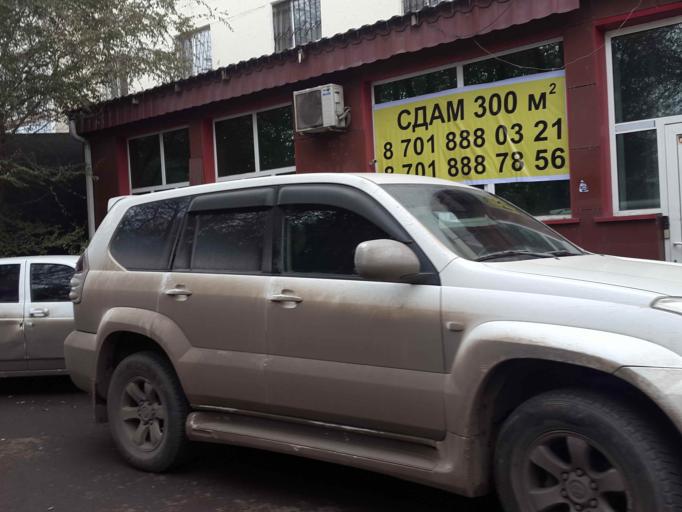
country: KZ
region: Astana Qalasy
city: Astana
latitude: 51.1549
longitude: 71.4709
